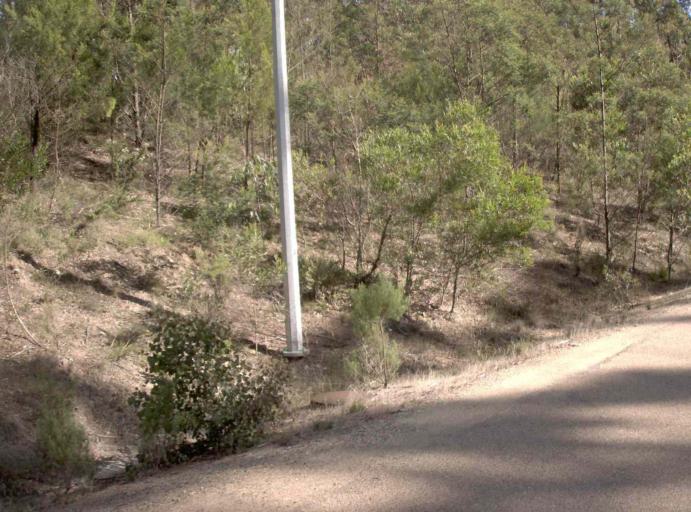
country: AU
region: Victoria
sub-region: East Gippsland
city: Lakes Entrance
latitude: -37.6910
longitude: 148.0420
